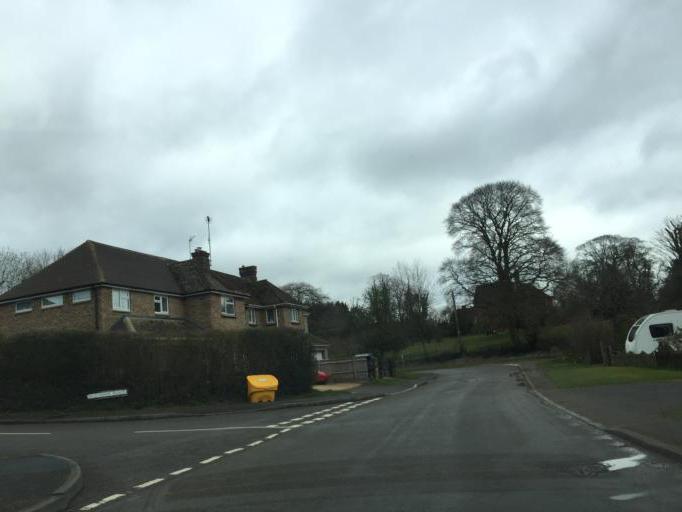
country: GB
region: England
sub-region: Northamptonshire
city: Silverstone
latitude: 52.0719
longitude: -1.0832
